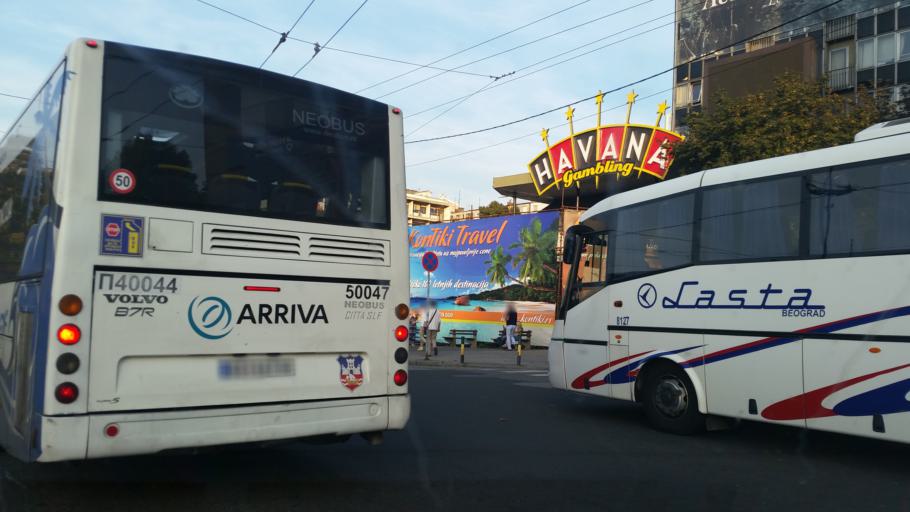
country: RS
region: Central Serbia
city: Belgrade
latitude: 44.8022
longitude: 20.4665
